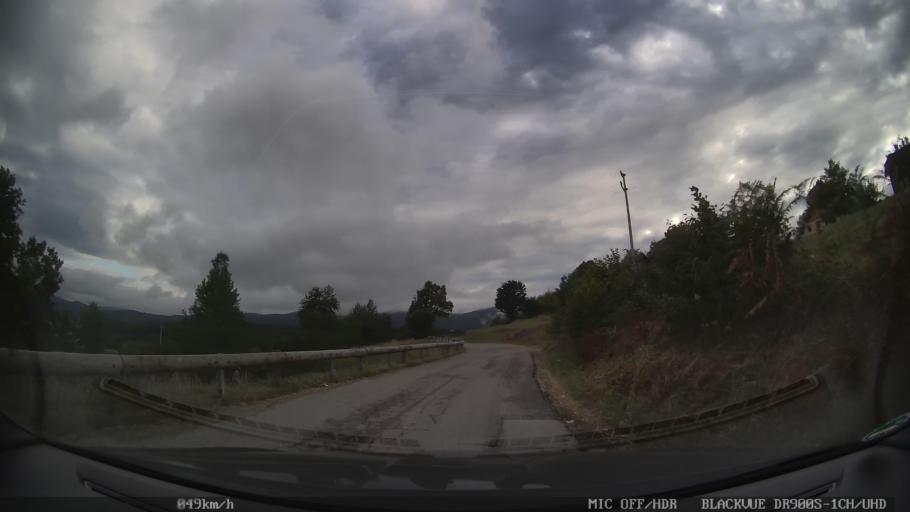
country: HR
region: Licko-Senjska
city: Jezerce
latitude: 44.9243
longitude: 15.5978
